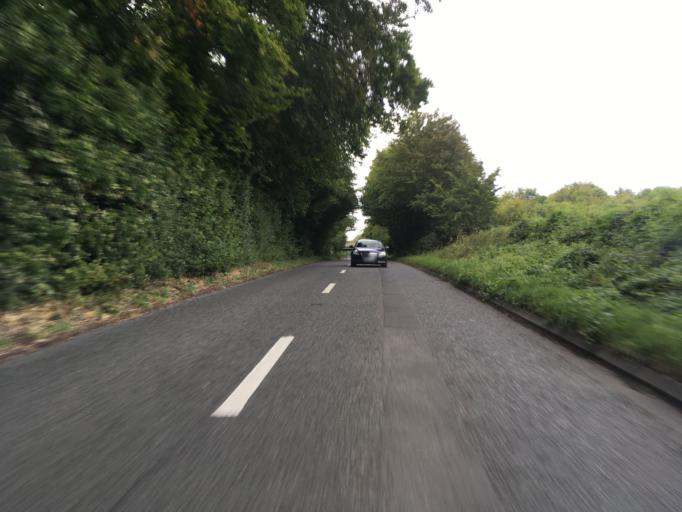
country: GB
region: England
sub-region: Hampshire
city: Overton
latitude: 51.1881
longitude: -1.2564
